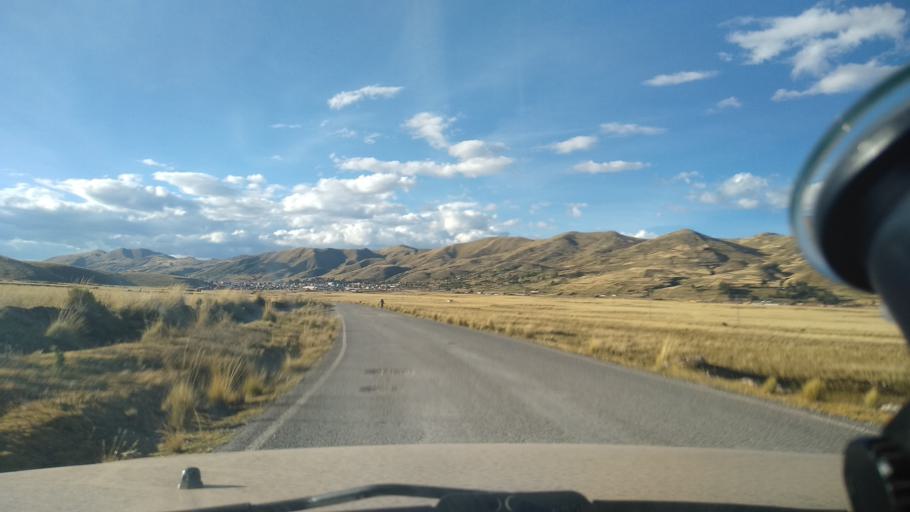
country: PE
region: Cusco
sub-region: Provincia de Canas
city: Chignayhua
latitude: -14.2420
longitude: -71.4331
